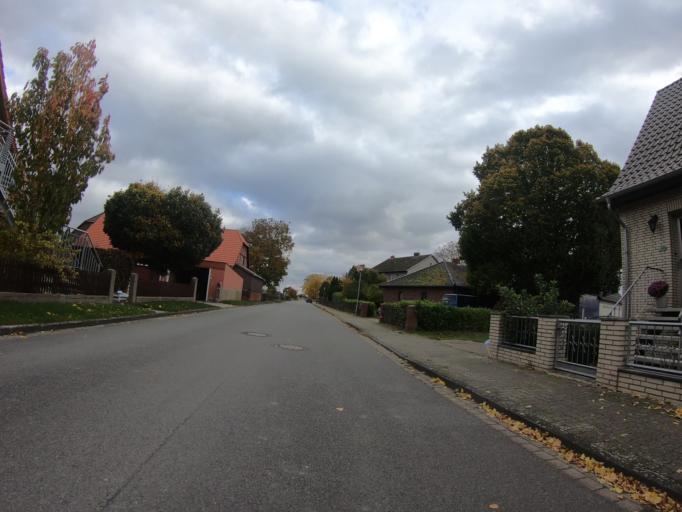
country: DE
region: Lower Saxony
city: Vordorf
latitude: 52.3776
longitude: 10.4873
